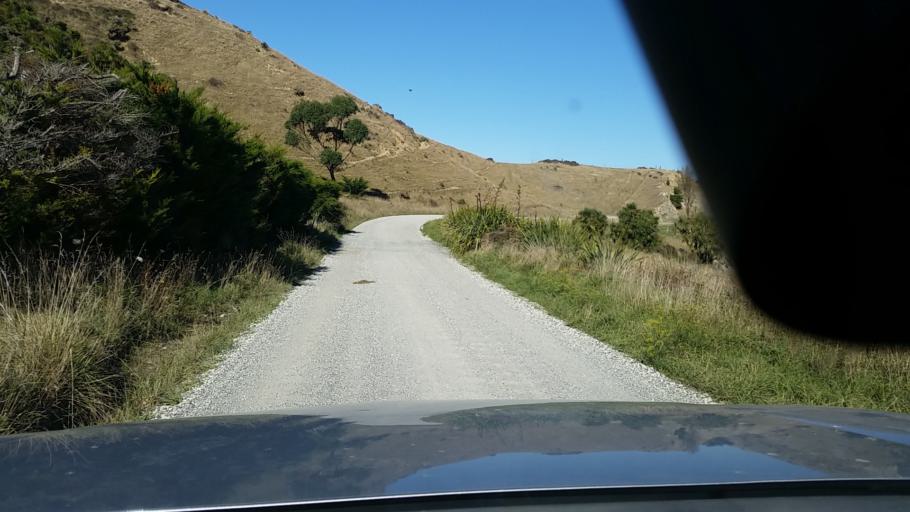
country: NZ
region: Marlborough
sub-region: Marlborough District
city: Blenheim
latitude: -41.8394
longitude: 174.1813
